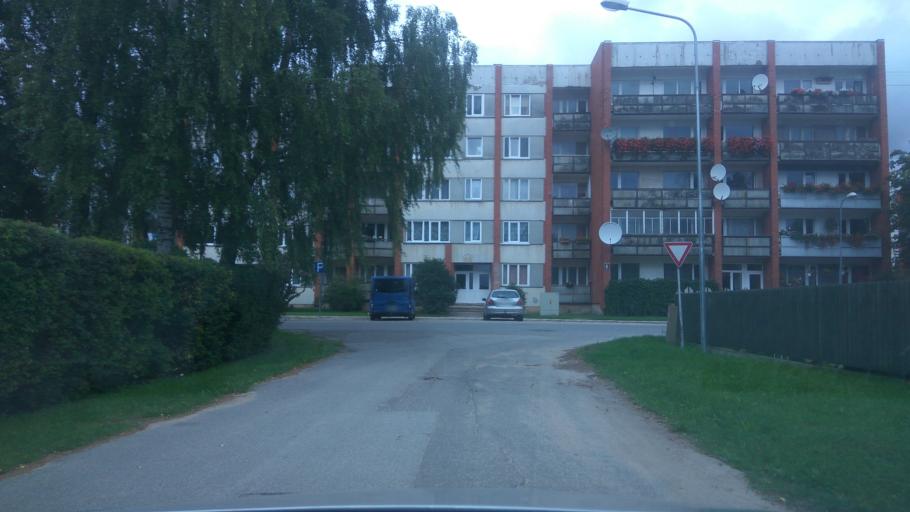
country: LV
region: Kuldigas Rajons
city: Kuldiga
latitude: 56.9727
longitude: 21.9533
